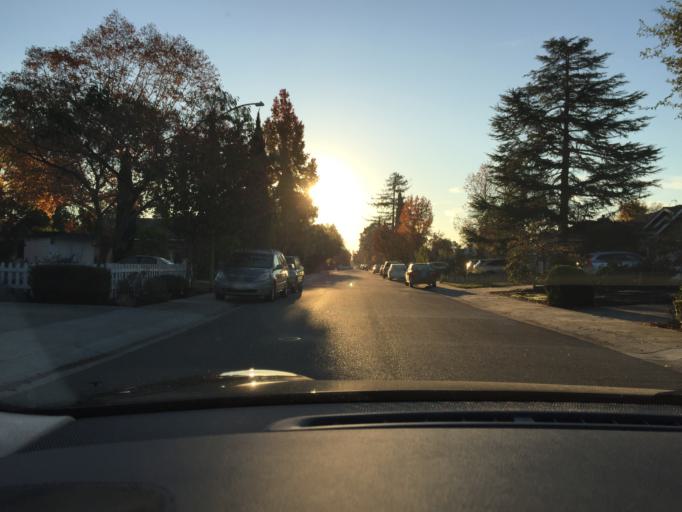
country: US
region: California
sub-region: Santa Clara County
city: Palo Alto
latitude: 37.4239
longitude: -122.1291
